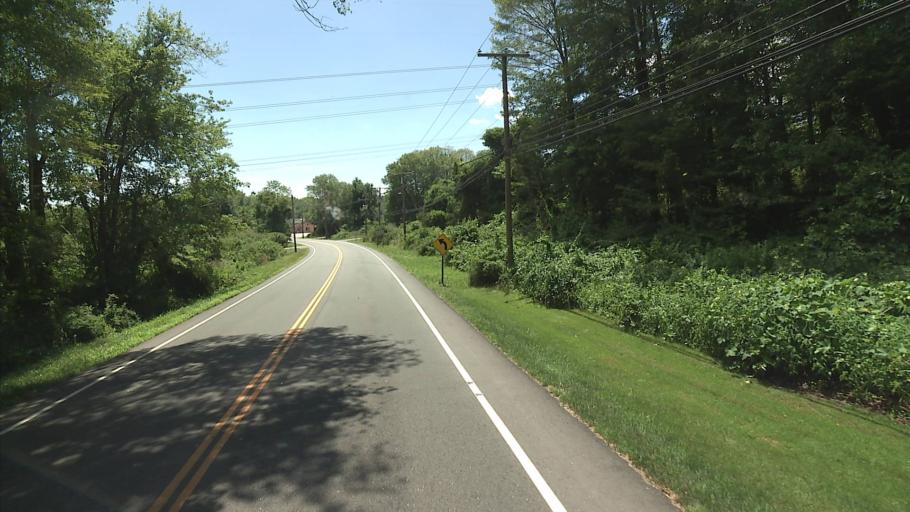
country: US
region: Connecticut
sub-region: Middlesex County
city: East Haddam
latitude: 41.4664
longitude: -72.4446
